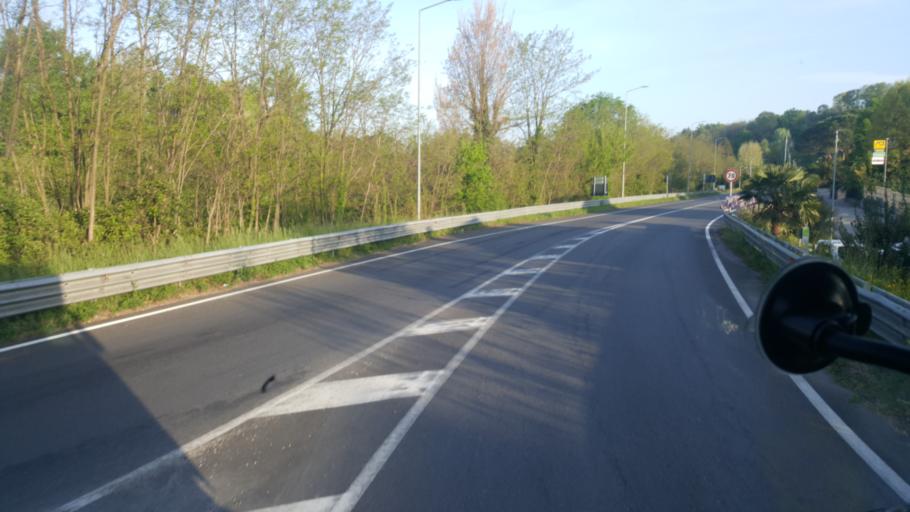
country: IT
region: Lombardy
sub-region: Provincia di Varese
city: Barasso
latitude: 45.8148
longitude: 8.7621
